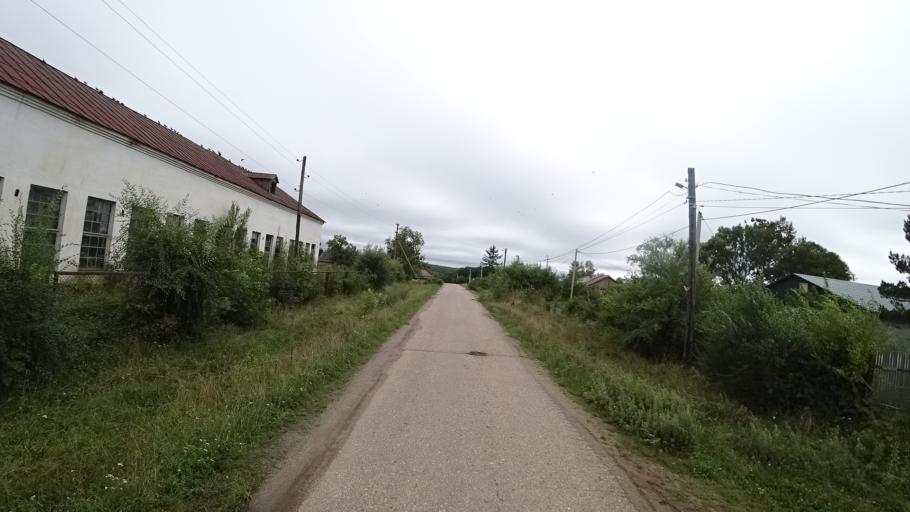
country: RU
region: Primorskiy
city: Monastyrishche
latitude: 44.0811
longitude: 132.5827
